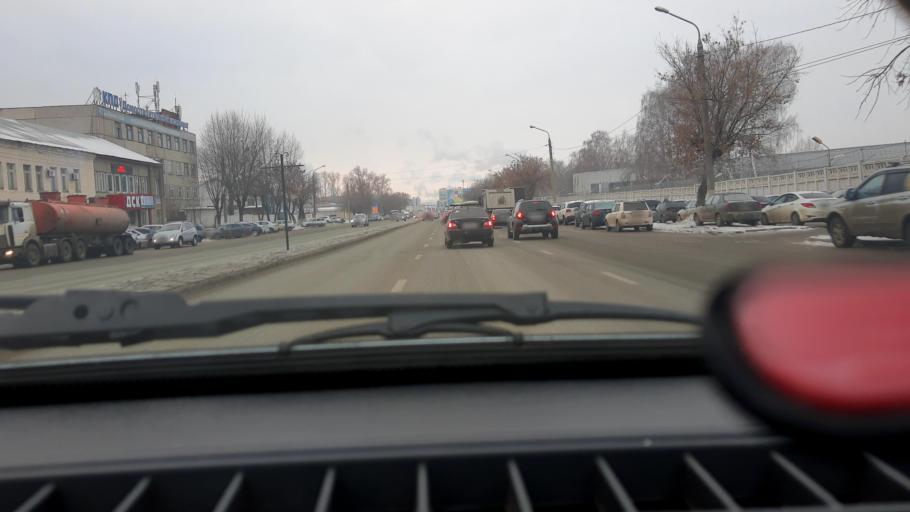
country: RU
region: Bashkortostan
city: Ufa
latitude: 54.8020
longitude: 56.0818
